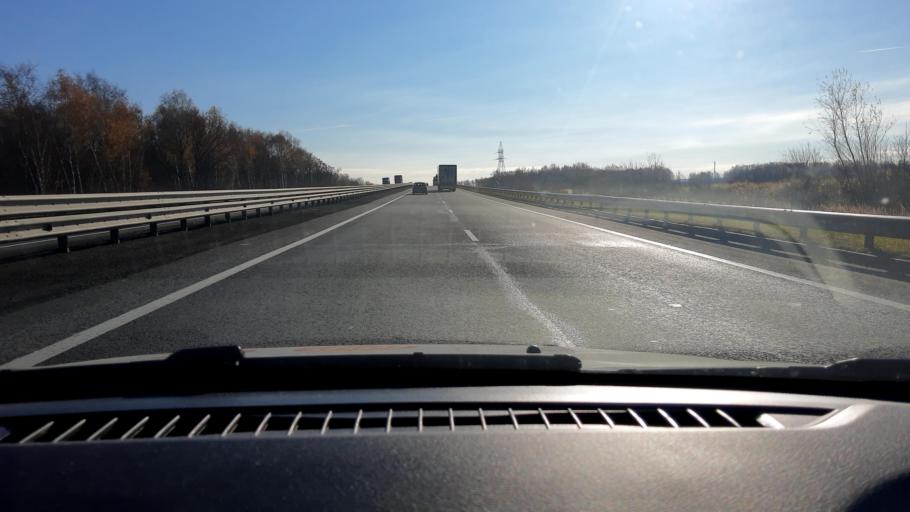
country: RU
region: Nizjnij Novgorod
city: Burevestnik
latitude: 56.1386
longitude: 43.7650
